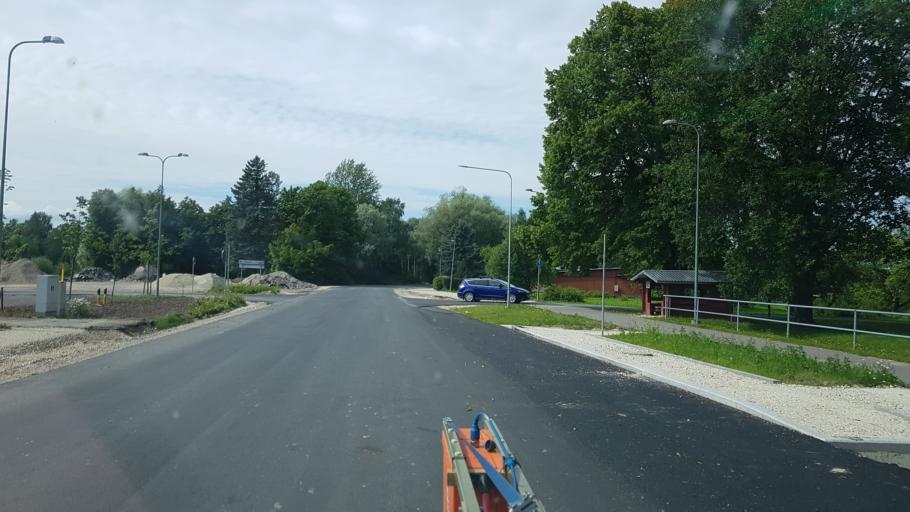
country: EE
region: Viljandimaa
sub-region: Suure-Jaani vald
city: Suure-Jaani
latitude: 58.5388
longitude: 25.4963
